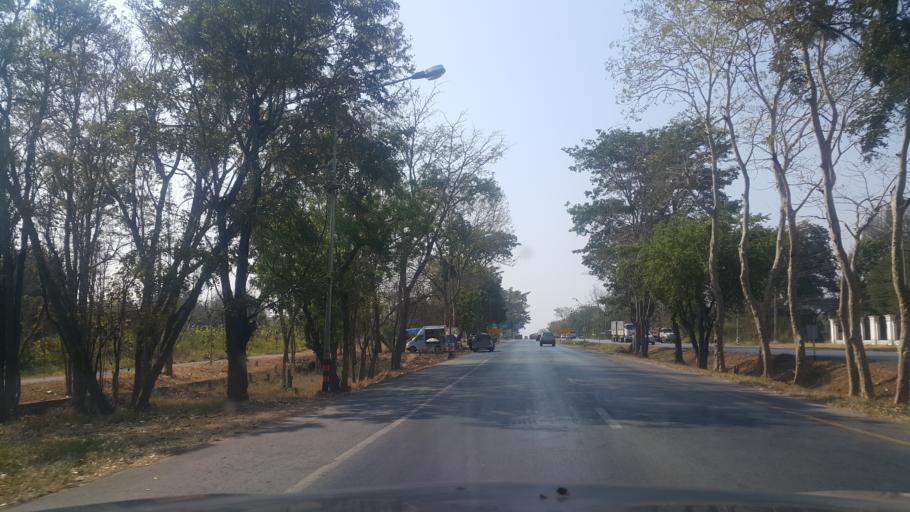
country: TH
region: Nakhon Ratchasima
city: Nakhon Ratchasima
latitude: 14.8657
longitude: 102.0714
